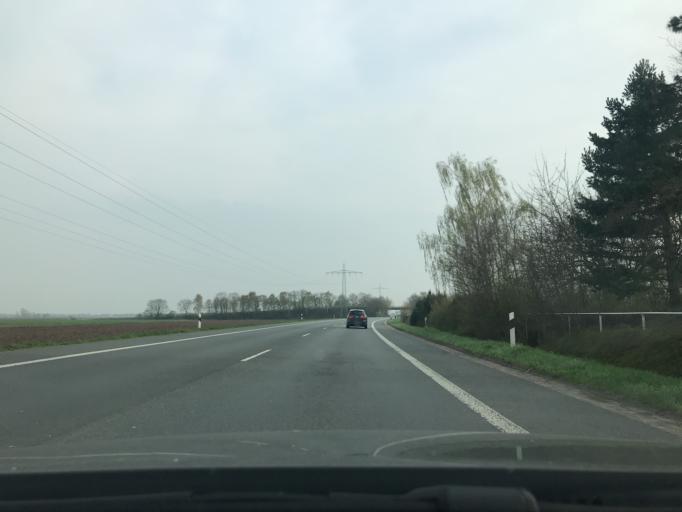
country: DE
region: North Rhine-Westphalia
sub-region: Regierungsbezirk Dusseldorf
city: Wachtendonk
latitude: 51.4581
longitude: 6.3825
